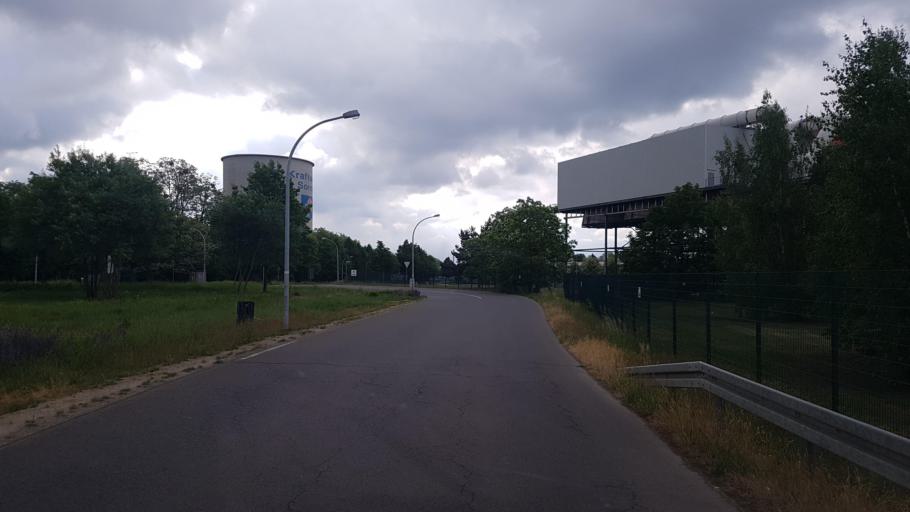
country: DE
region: Brandenburg
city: Grossraschen
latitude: 51.5824
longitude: 13.9764
